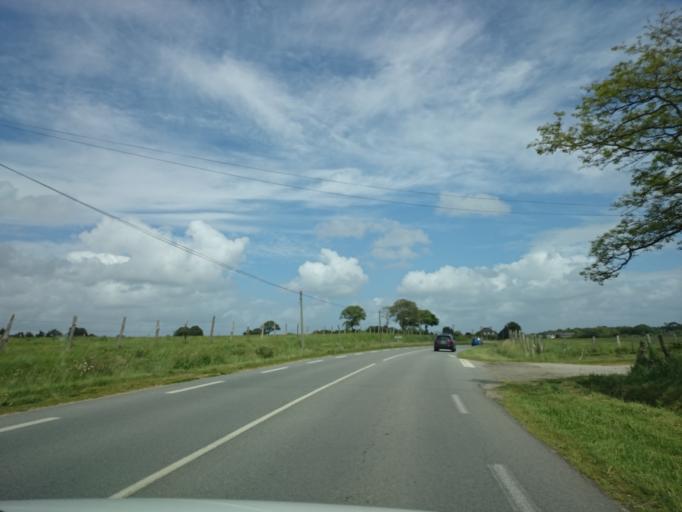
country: FR
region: Brittany
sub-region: Departement du Morbihan
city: Arradon
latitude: 47.6366
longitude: -2.8371
